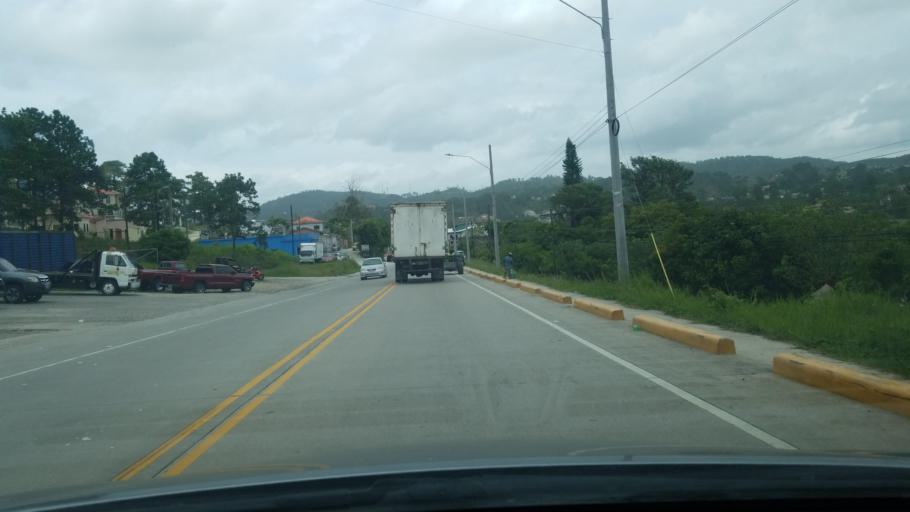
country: HN
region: Copan
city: Santa Rosa de Copan
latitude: 14.7888
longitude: -88.7797
